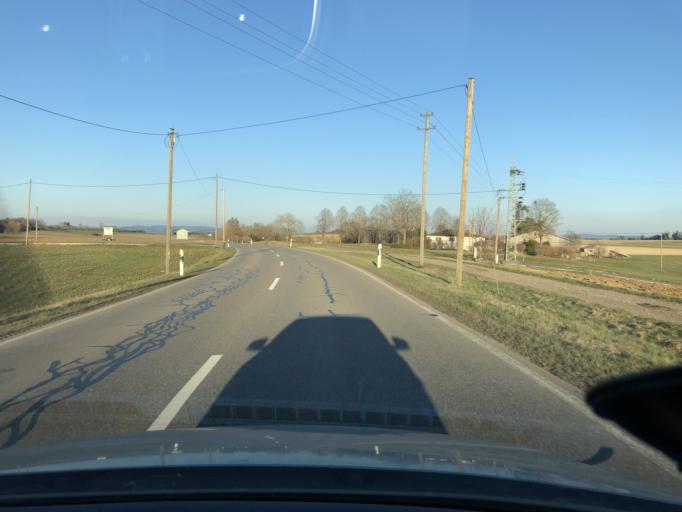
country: DE
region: Baden-Wuerttemberg
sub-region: Freiburg Region
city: Bonndorf im Schwarzwald
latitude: 47.8206
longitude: 8.3691
